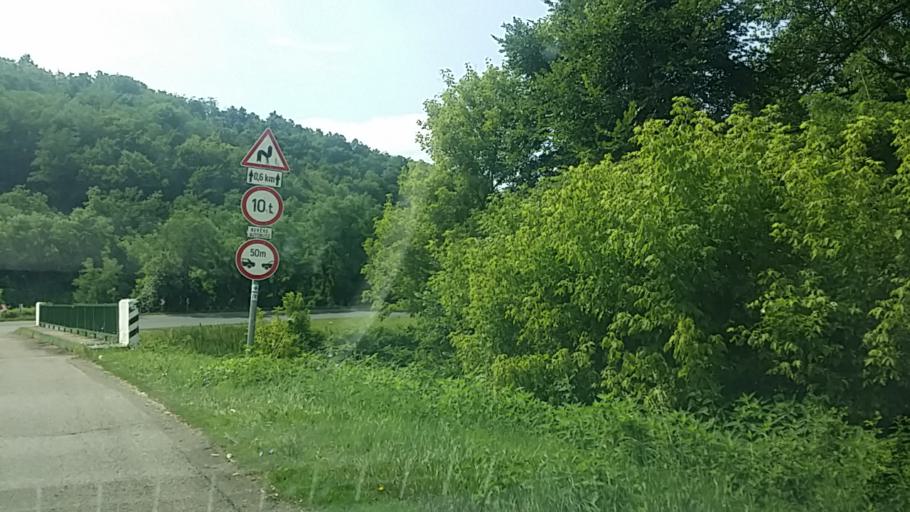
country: HU
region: Nograd
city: Tar
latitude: 47.9606
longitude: 19.7539
